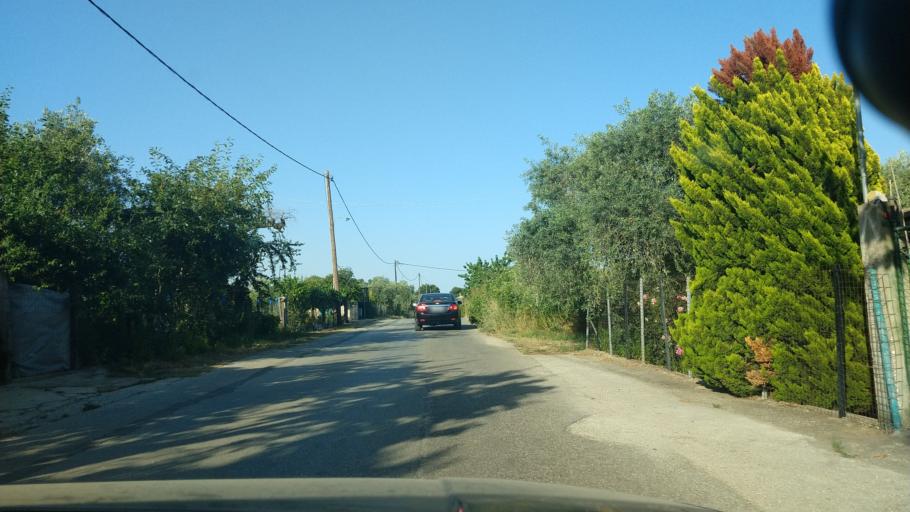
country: GR
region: East Macedonia and Thrace
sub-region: Nomos Kavalas
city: Potamia
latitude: 40.7183
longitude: 24.7495
